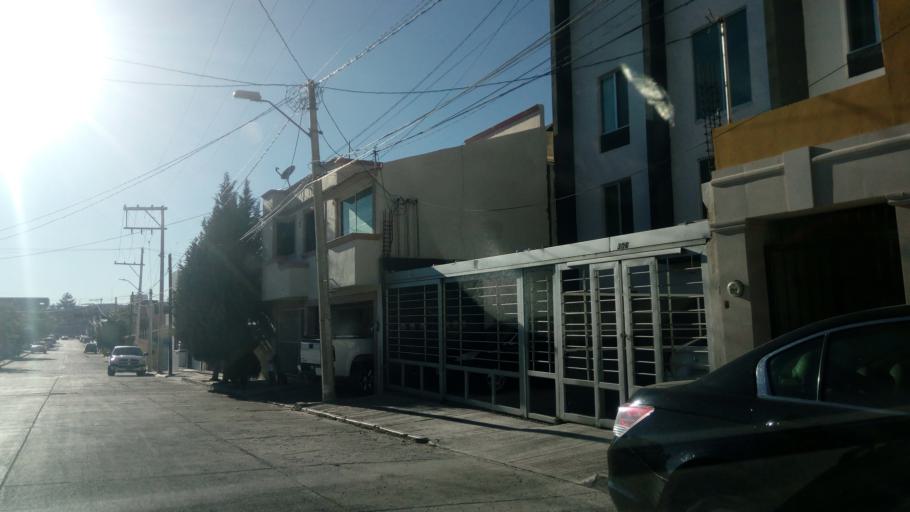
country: MX
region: Durango
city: Victoria de Durango
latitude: 24.0212
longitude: -104.6874
